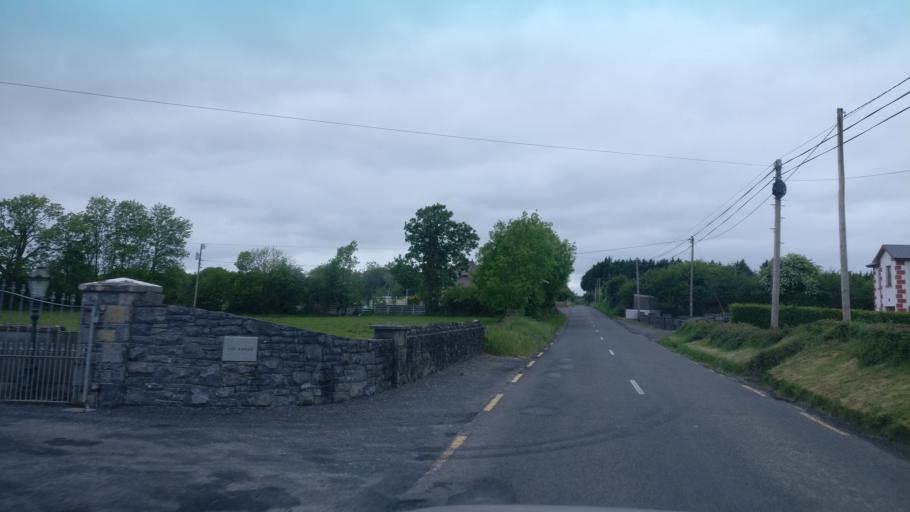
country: IE
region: Connaught
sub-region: County Galway
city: Portumna
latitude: 53.0975
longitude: -8.2452
